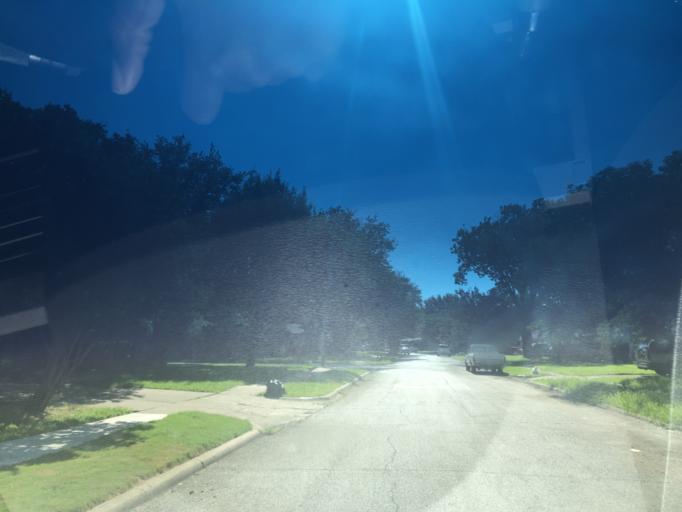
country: US
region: Texas
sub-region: Dallas County
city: Grand Prairie
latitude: 32.7147
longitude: -97.0107
